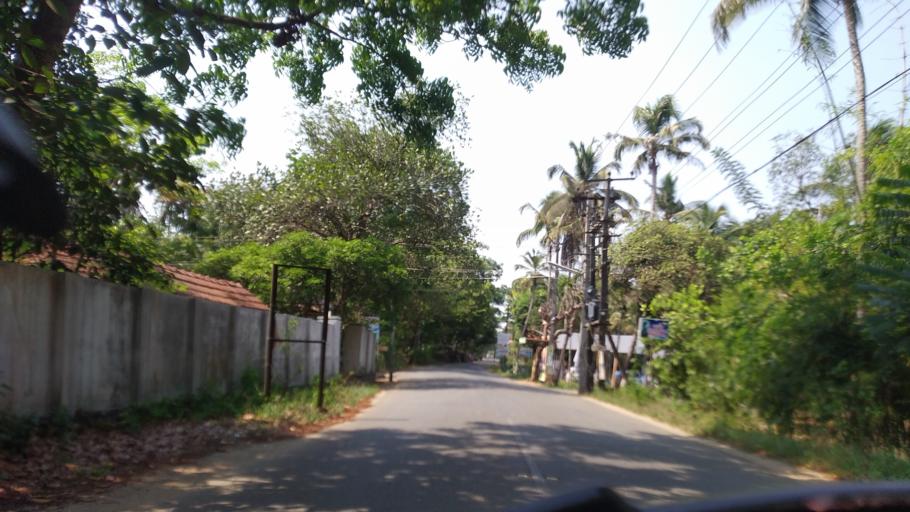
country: IN
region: Kerala
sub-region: Thrissur District
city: Kodungallur
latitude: 10.2527
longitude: 76.1475
